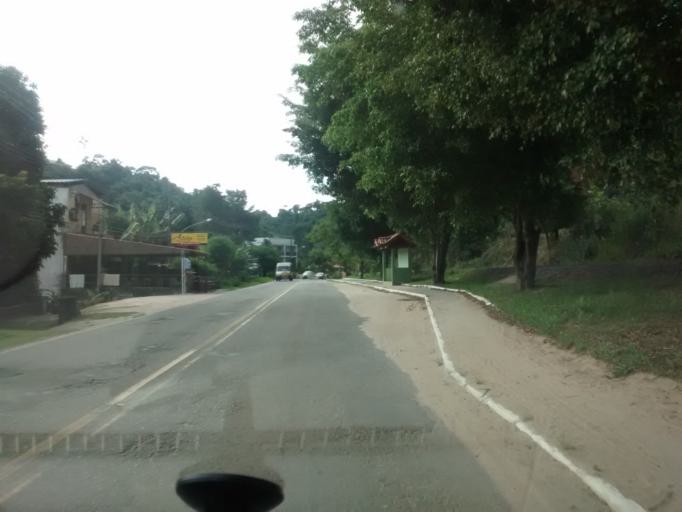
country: BR
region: Rio de Janeiro
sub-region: Miguel Pereira
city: Miguel Pereira
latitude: -22.4673
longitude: -43.4886
